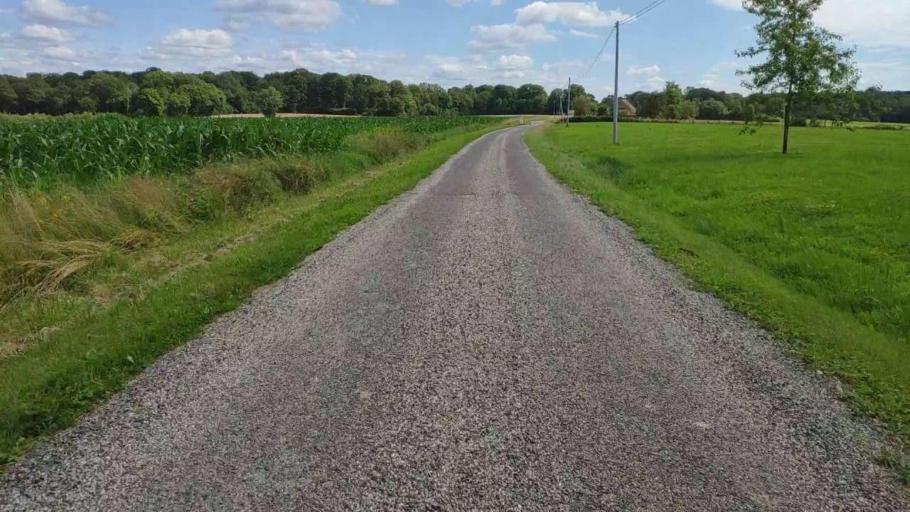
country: FR
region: Franche-Comte
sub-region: Departement du Jura
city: Bletterans
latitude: 46.8127
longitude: 5.4274
